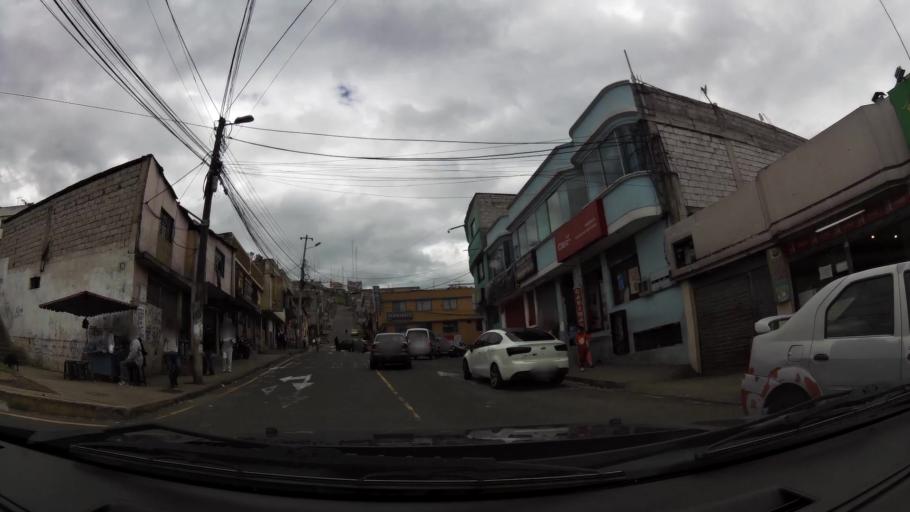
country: EC
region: Pichincha
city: Quito
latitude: -0.2551
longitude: -78.5043
